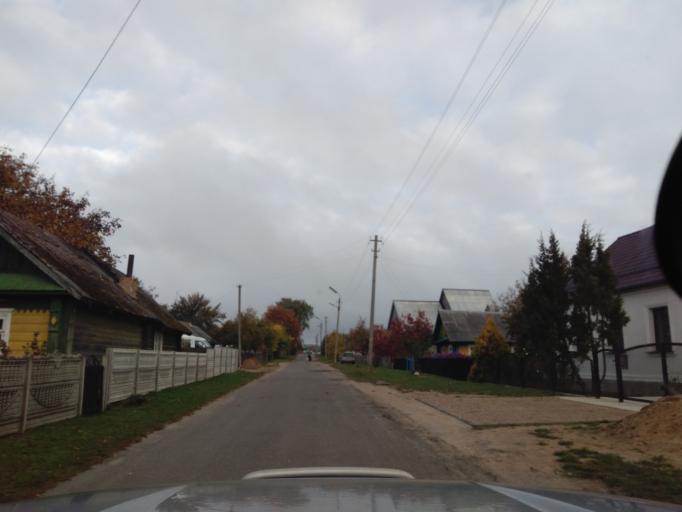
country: BY
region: Minsk
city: Kapyl'
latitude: 53.1585
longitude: 27.0837
